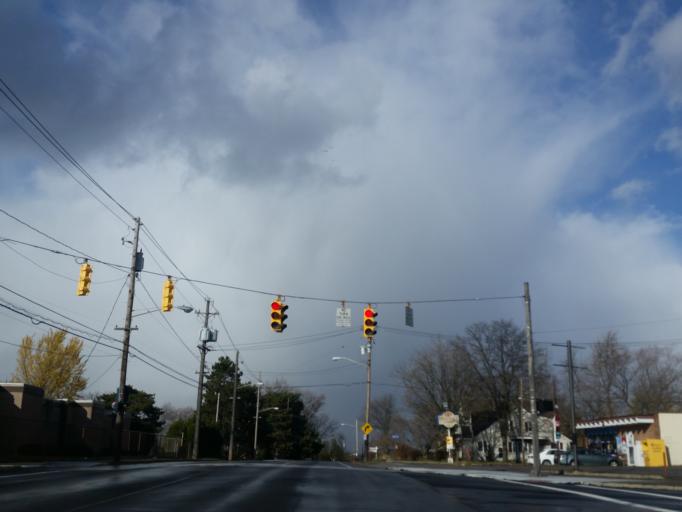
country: US
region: Ohio
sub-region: Cuyahoga County
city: Brooklyn Heights
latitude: 41.4294
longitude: -81.6972
